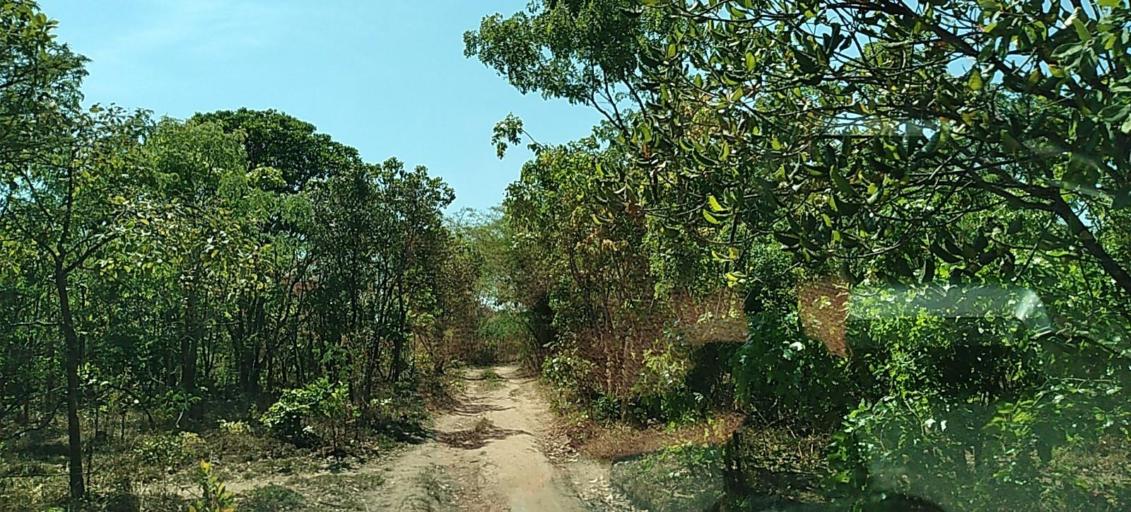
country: ZM
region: Copperbelt
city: Chililabombwe
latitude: -12.2861
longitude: 27.8837
